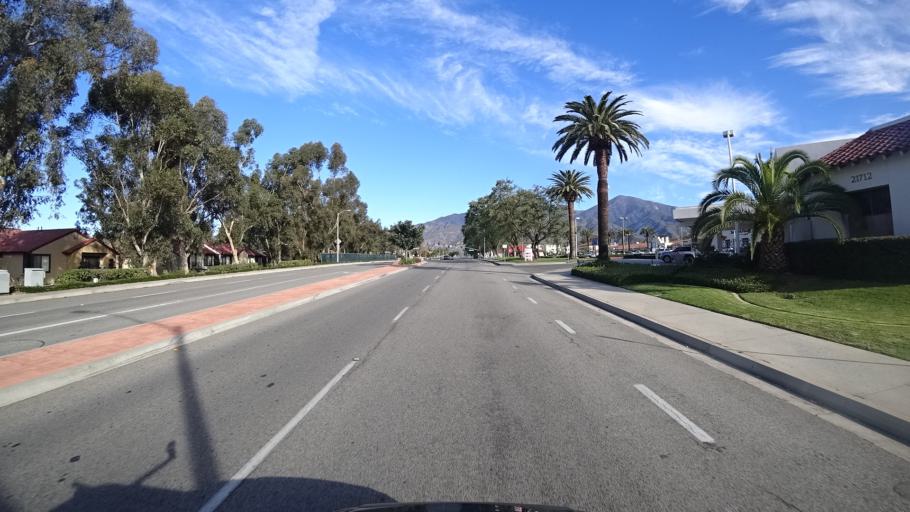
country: US
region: California
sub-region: Orange County
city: Trabuco Canyon
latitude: 33.6468
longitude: -117.5776
